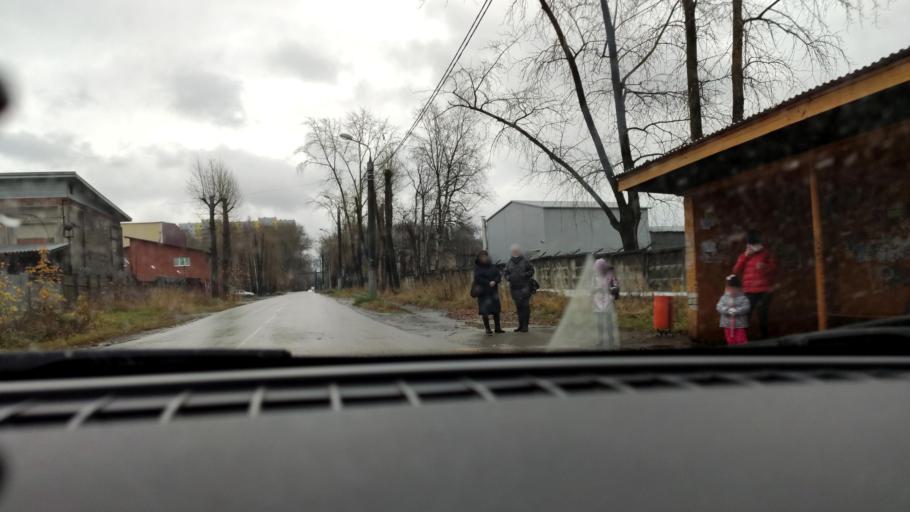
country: RU
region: Perm
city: Perm
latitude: 58.0966
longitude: 56.3709
